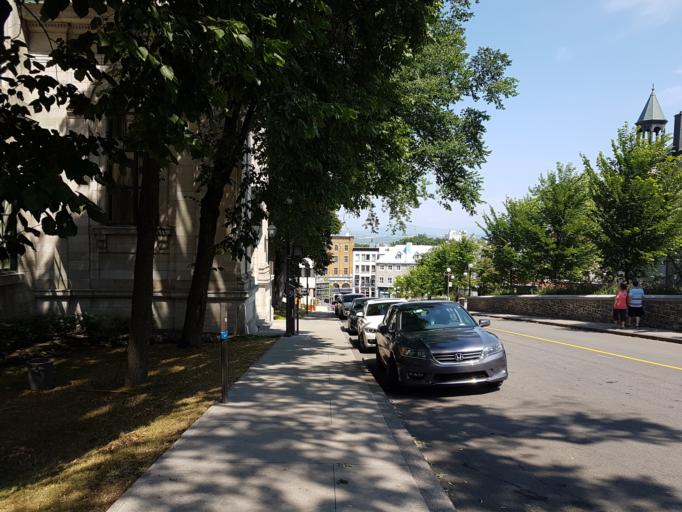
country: CA
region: Quebec
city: Quebec
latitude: 46.8133
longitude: -71.2088
